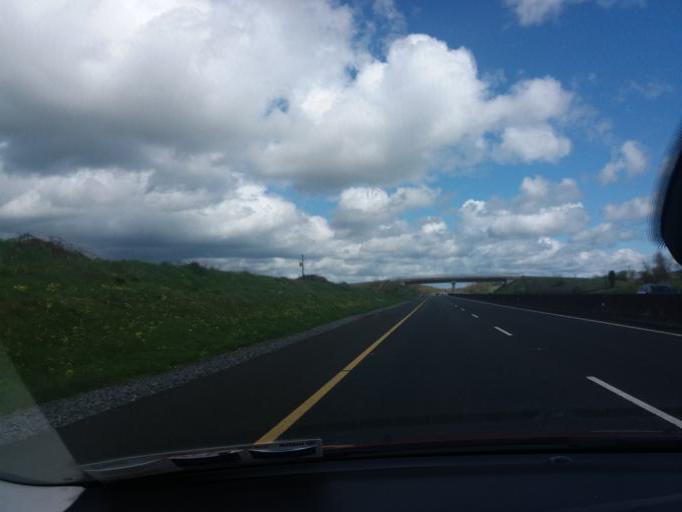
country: IE
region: Leinster
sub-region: Laois
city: Rathdowney
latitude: 52.7880
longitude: -7.5245
